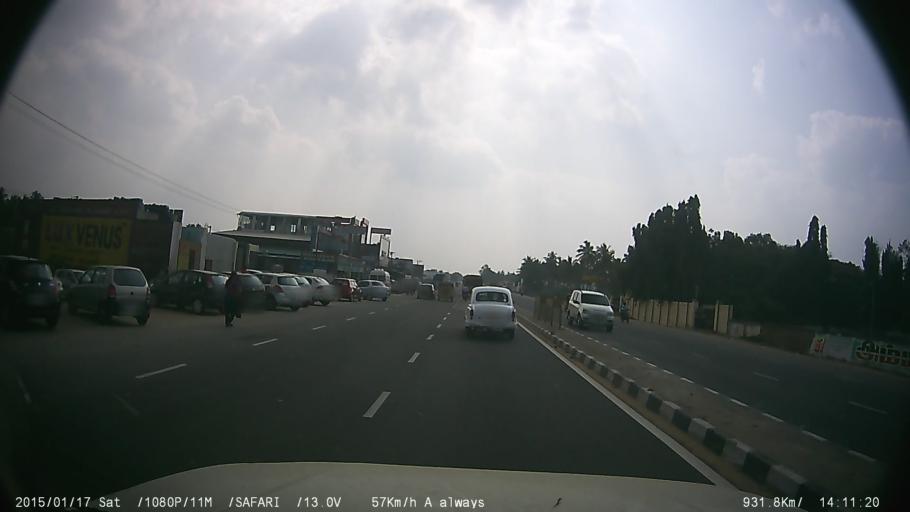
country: IN
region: Tamil Nadu
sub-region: Vellore
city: Ambur
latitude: 12.7964
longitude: 78.7311
